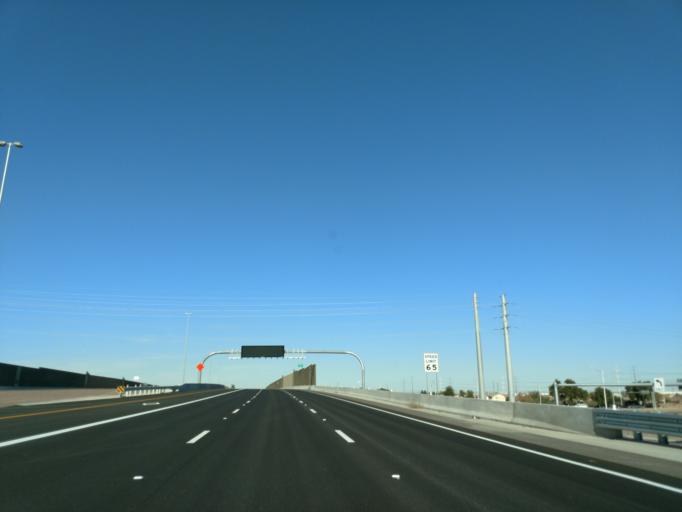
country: US
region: Arizona
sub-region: Maricopa County
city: Laveen
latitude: 33.4063
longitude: -112.1917
